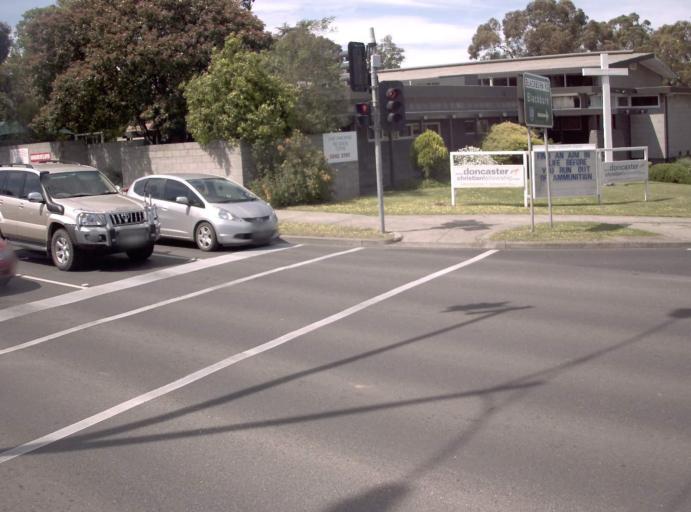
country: AU
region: Victoria
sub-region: Manningham
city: Donvale
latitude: -37.7892
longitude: 145.1620
